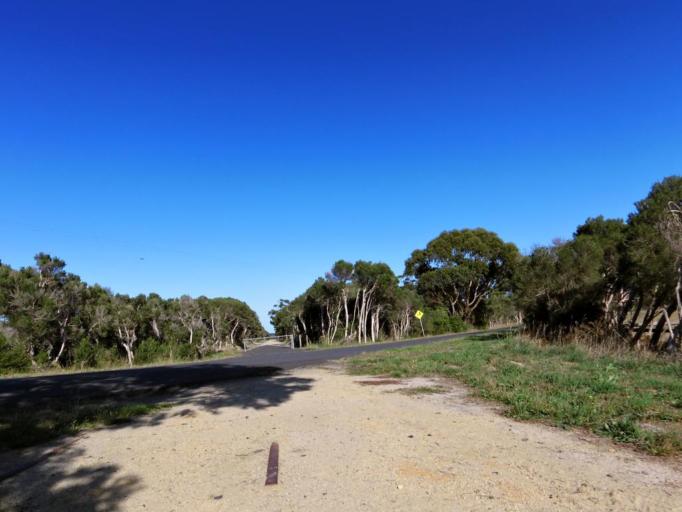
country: AU
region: Victoria
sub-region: Bass Coast
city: North Wonthaggi
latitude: -38.5043
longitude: 145.4952
